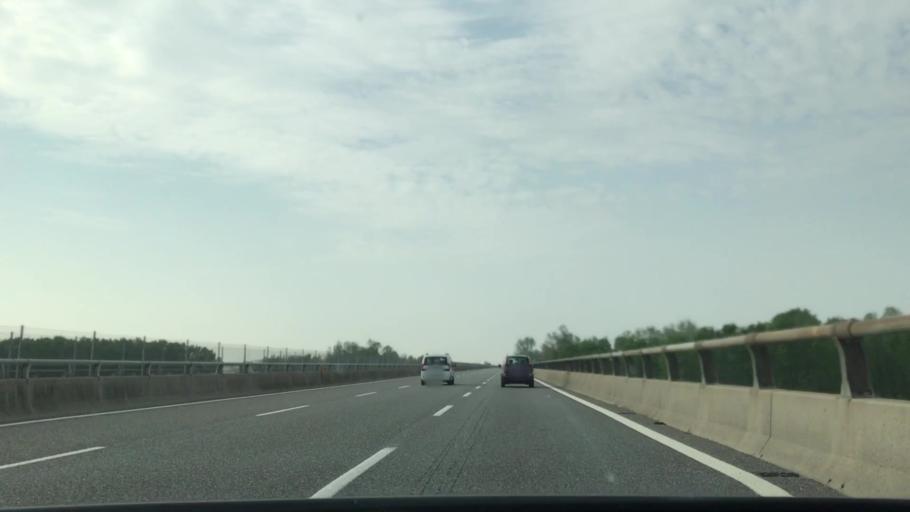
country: IT
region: Piedmont
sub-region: Provincia di Vercelli
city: Prarolo
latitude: 45.3085
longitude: 8.4704
